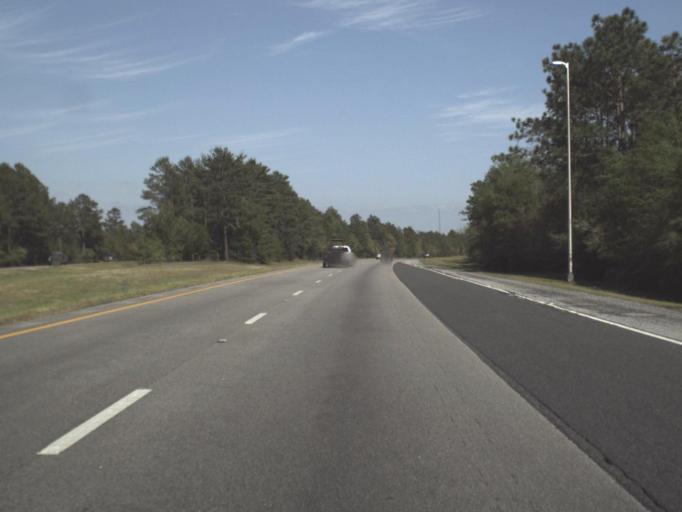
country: US
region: Florida
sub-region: Okaloosa County
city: Crestview
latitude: 30.7266
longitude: -86.5000
